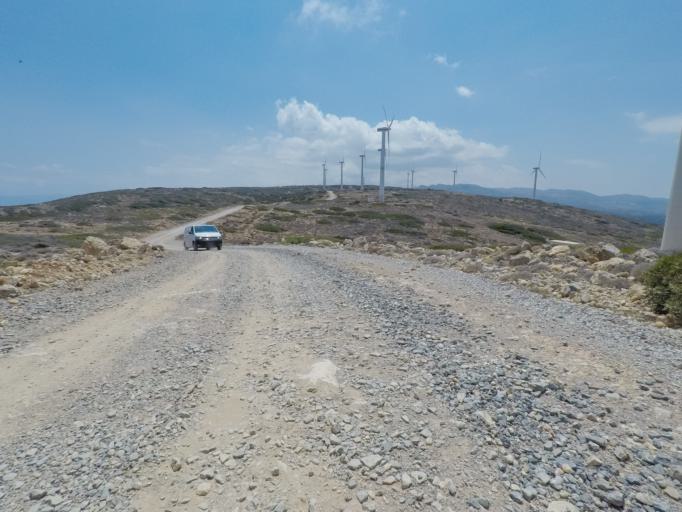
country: GR
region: Crete
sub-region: Nomos Lasithiou
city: Elounda
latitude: 35.3308
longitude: 25.7596
